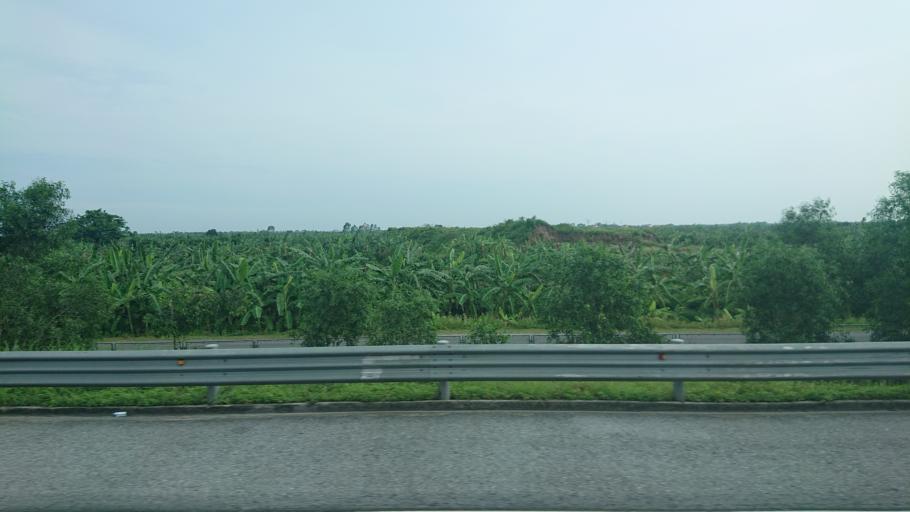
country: VN
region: Hai Duong
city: Tu Ky
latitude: 20.8223
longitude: 106.4723
